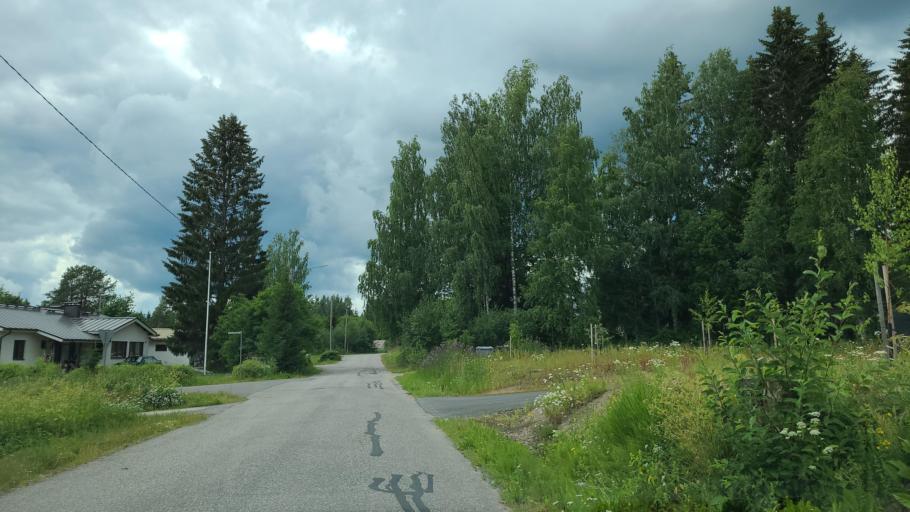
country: FI
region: Northern Savo
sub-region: Koillis-Savo
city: Kaavi
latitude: 62.9723
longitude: 28.4850
